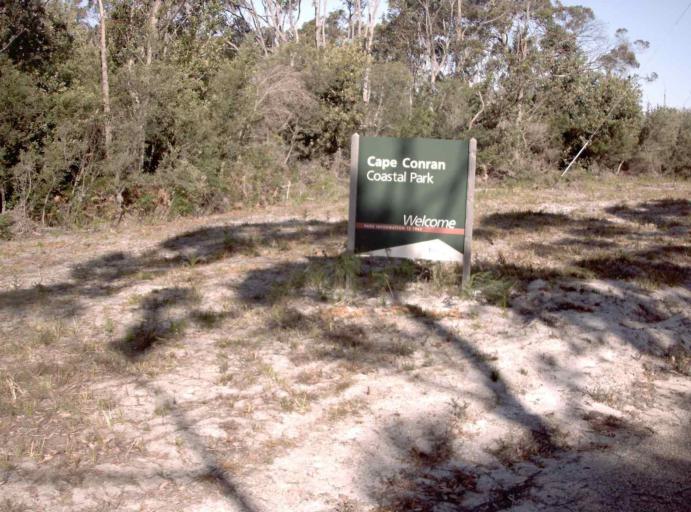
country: AU
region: Victoria
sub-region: East Gippsland
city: Lakes Entrance
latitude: -37.7982
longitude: 148.7197
